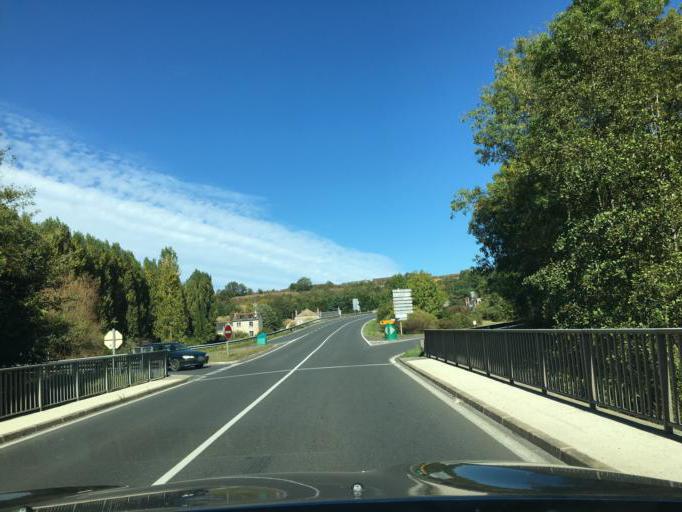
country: FR
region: Centre
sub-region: Departement d'Indre-et-Loire
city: Azay-le-Rideau
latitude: 47.2611
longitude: 0.4576
